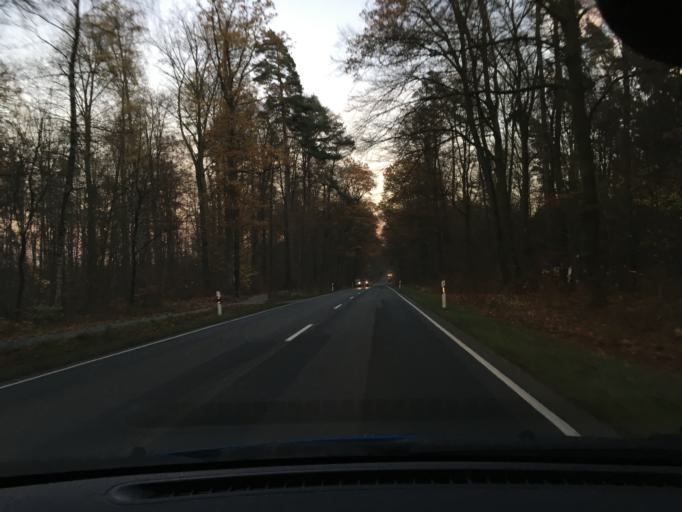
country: DE
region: Lower Saxony
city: Uelzen
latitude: 52.9797
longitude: 10.5334
